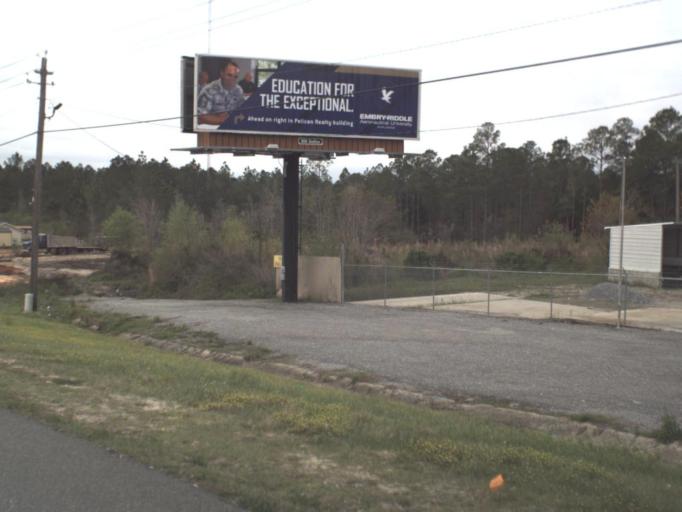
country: US
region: Florida
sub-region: Okaloosa County
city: Crestview
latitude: 30.7141
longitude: -86.5700
